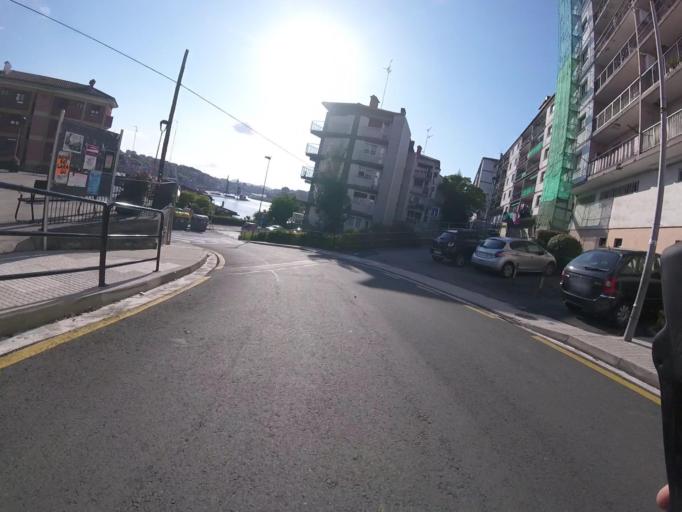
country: ES
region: Basque Country
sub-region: Provincia de Guipuzcoa
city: Pasaia
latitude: 43.3242
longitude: -1.9149
